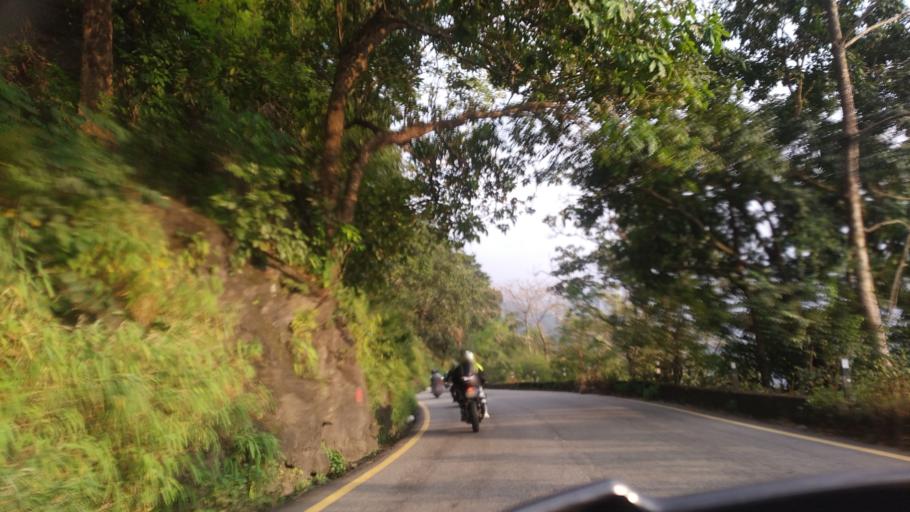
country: IN
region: Kerala
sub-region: Wayanad
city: Kalpetta
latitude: 11.5113
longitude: 76.0165
